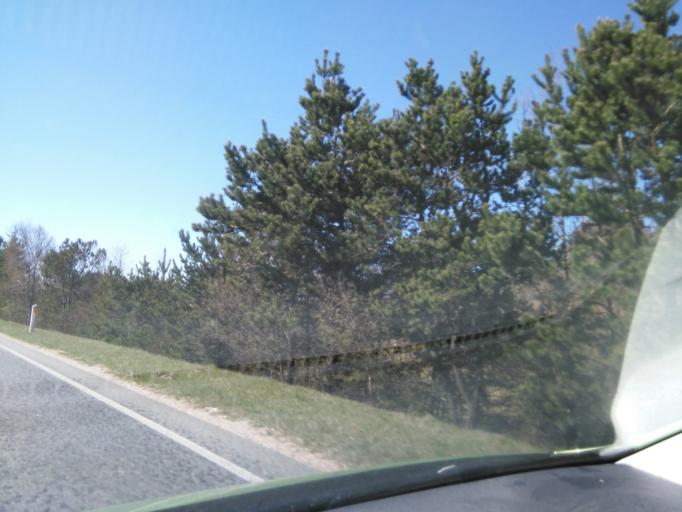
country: DK
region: South Denmark
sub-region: Varde Kommune
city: Oksbol
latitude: 55.6146
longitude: 8.2349
